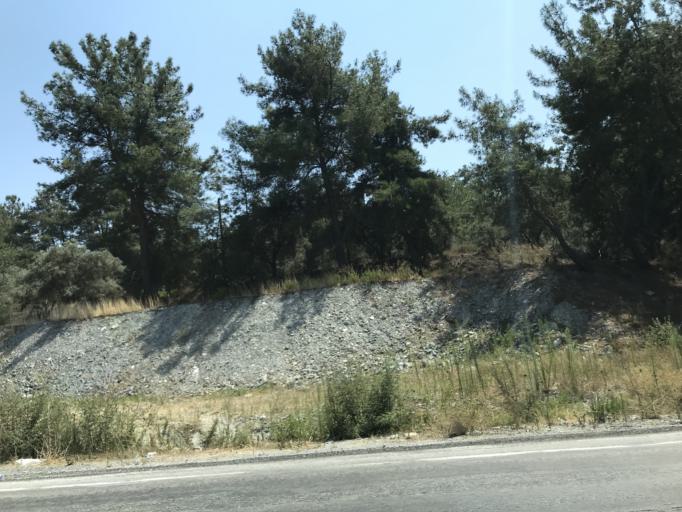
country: TR
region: Izmir
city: Selcuk
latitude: 37.8887
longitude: 27.3713
